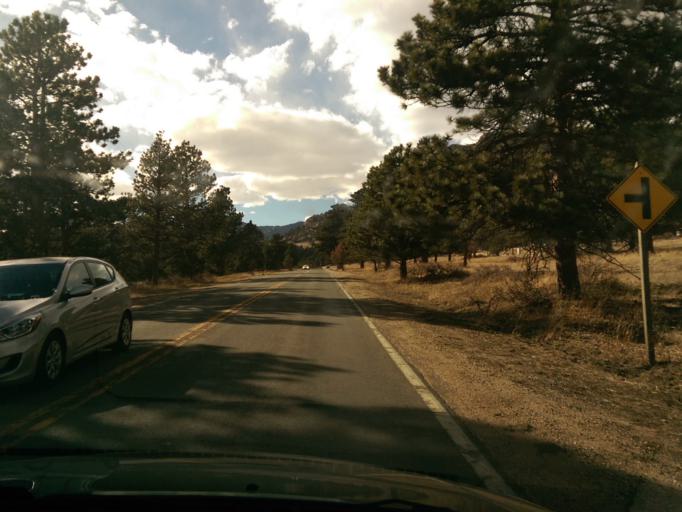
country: US
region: Colorado
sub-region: Larimer County
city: Estes Park
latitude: 40.3656
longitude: -105.5556
